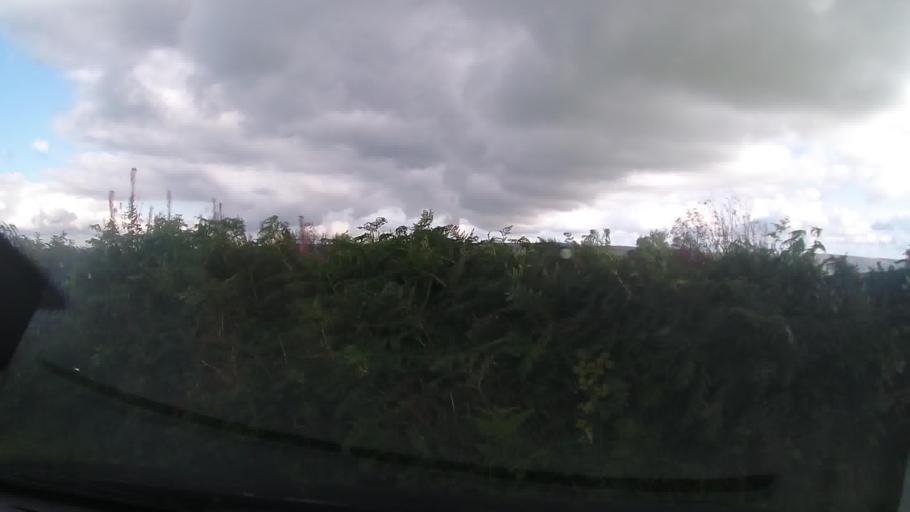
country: GB
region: England
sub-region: Shropshire
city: Norbury
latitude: 52.5737
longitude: -2.9317
